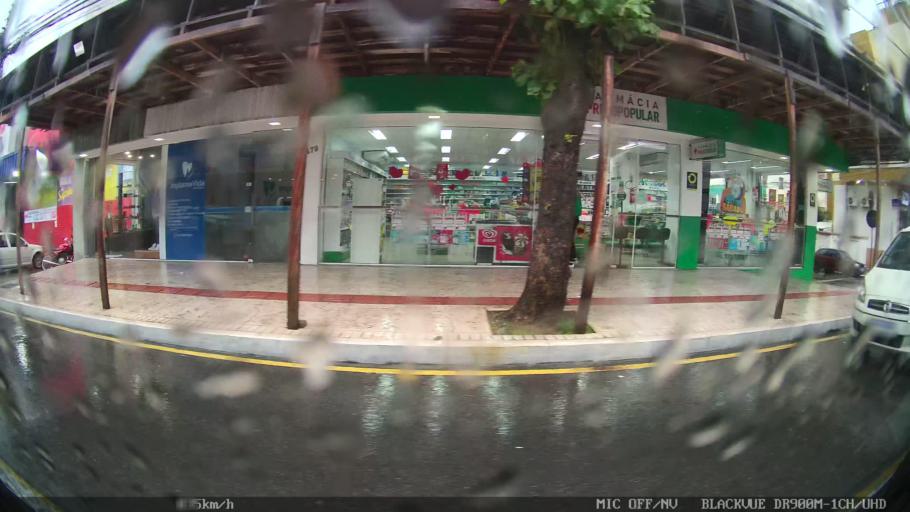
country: BR
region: Santa Catarina
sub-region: Balneario Camboriu
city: Balneario Camboriu
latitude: -26.9783
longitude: -48.6466
